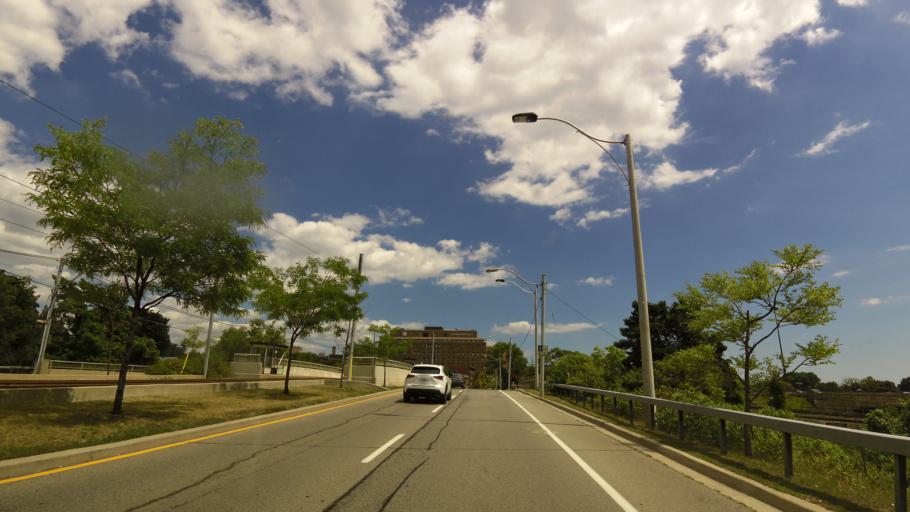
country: CA
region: Ontario
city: Toronto
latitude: 43.6396
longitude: -79.4548
